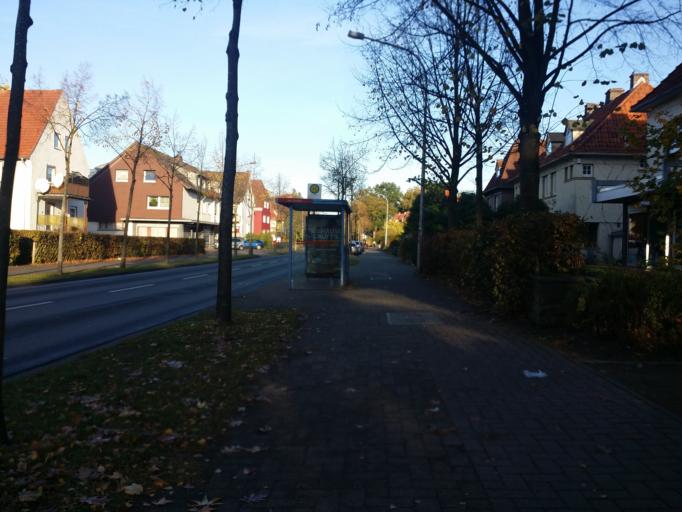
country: DE
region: Lower Saxony
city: Delmenhorst
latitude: 53.0386
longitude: 8.6401
